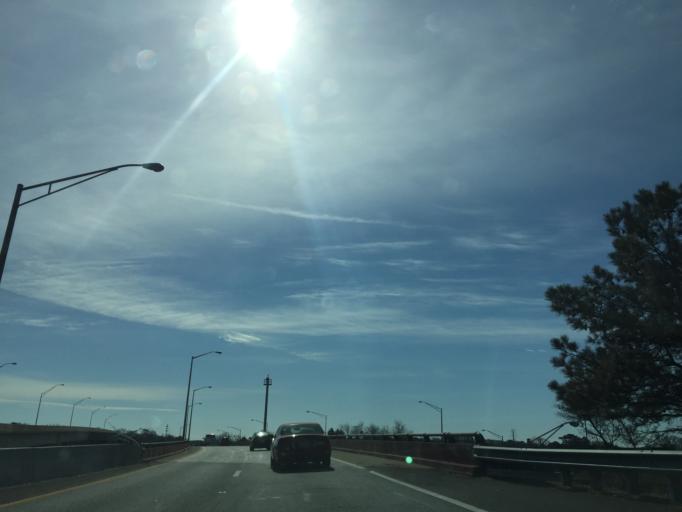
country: US
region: Virginia
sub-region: City of Norfolk
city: Norfolk
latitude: 36.9187
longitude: -76.2697
